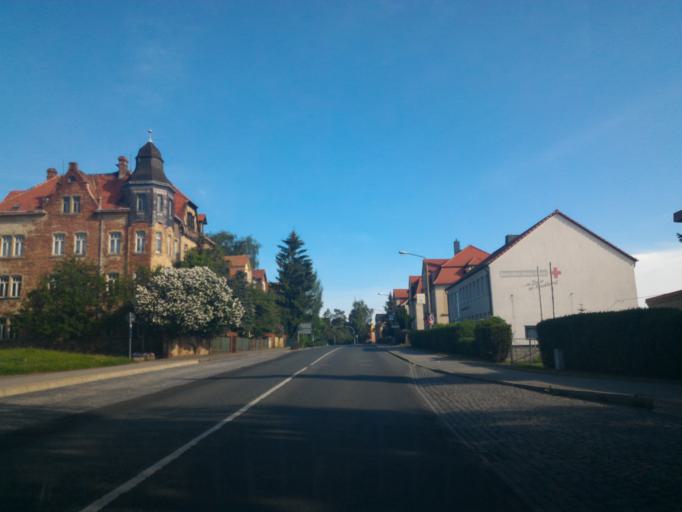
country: DE
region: Saxony
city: Lobau
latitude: 51.0885
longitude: 14.6704
